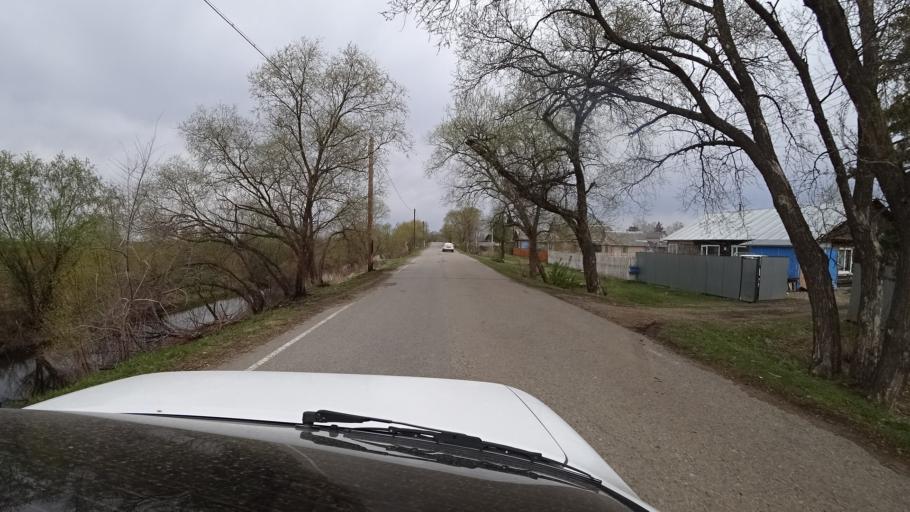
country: RU
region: Primorskiy
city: Dal'nerechensk
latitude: 45.9720
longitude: 133.7553
